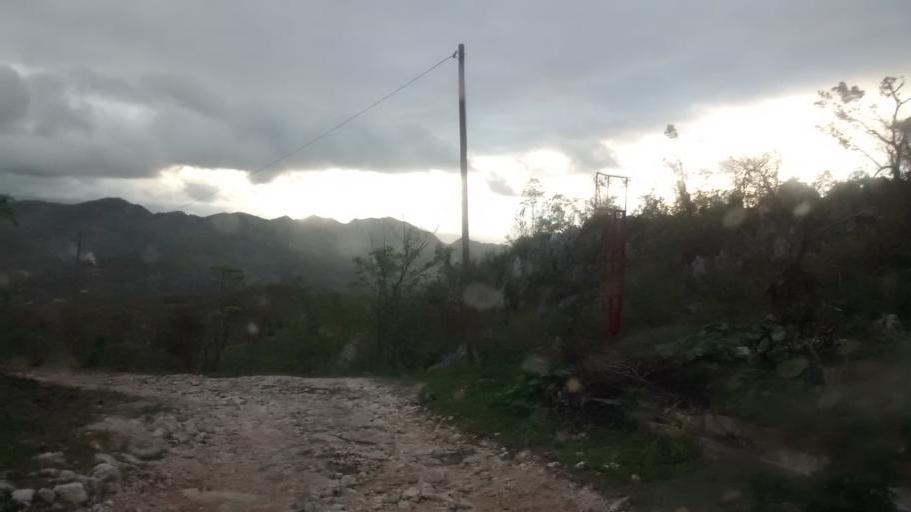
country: HT
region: Grandans
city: Corail
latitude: 18.4787
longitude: -73.7921
